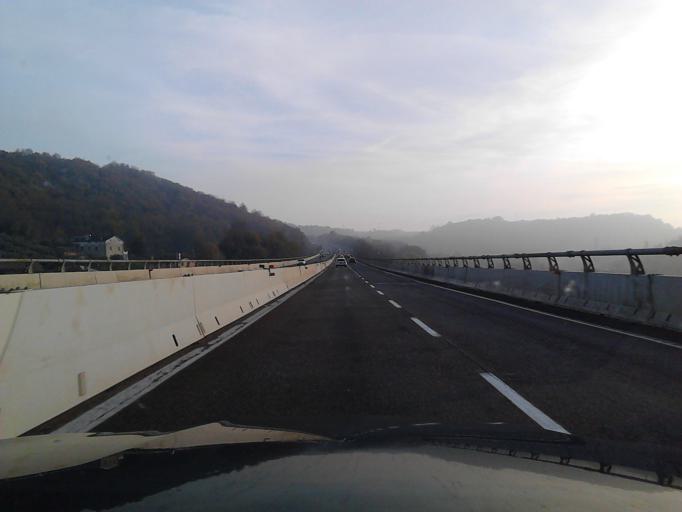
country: IT
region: Abruzzo
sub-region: Provincia di Chieti
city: San Vito Chietino
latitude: 42.2879
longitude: 14.4335
